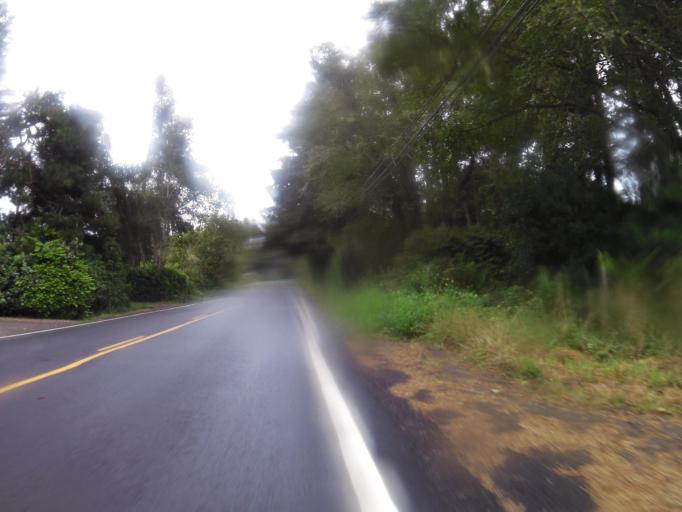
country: US
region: California
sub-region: Humboldt County
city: Westhaven-Moonstone
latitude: 41.1248
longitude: -124.1564
